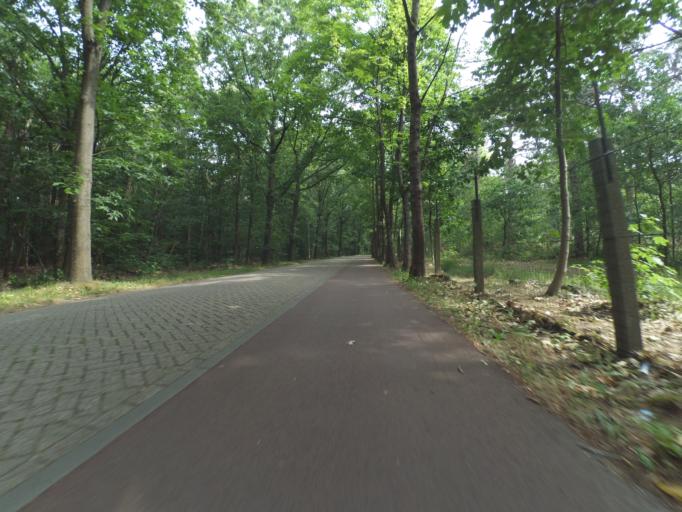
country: NL
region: North Brabant
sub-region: Gemeente Rucphen
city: Rucphen
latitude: 51.5655
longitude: 4.5569
